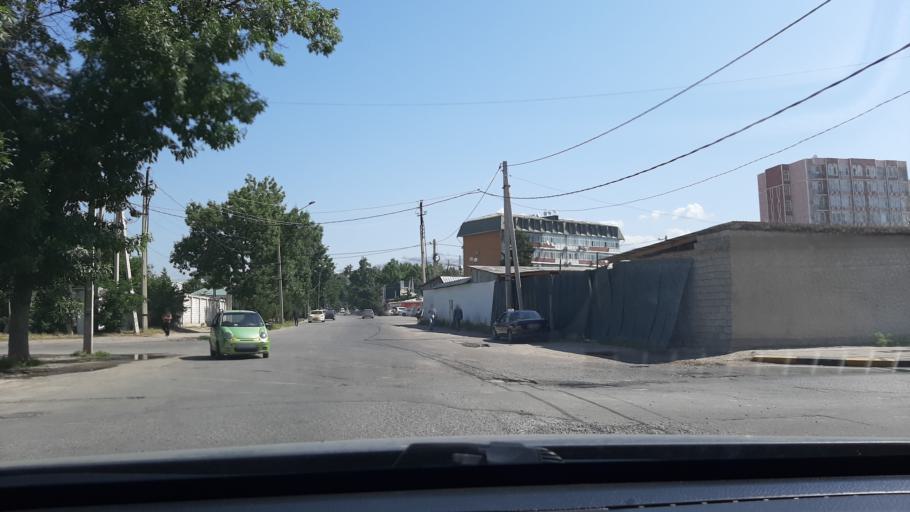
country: TJ
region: Dushanbe
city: Dushanbe
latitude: 38.5547
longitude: 68.7561
